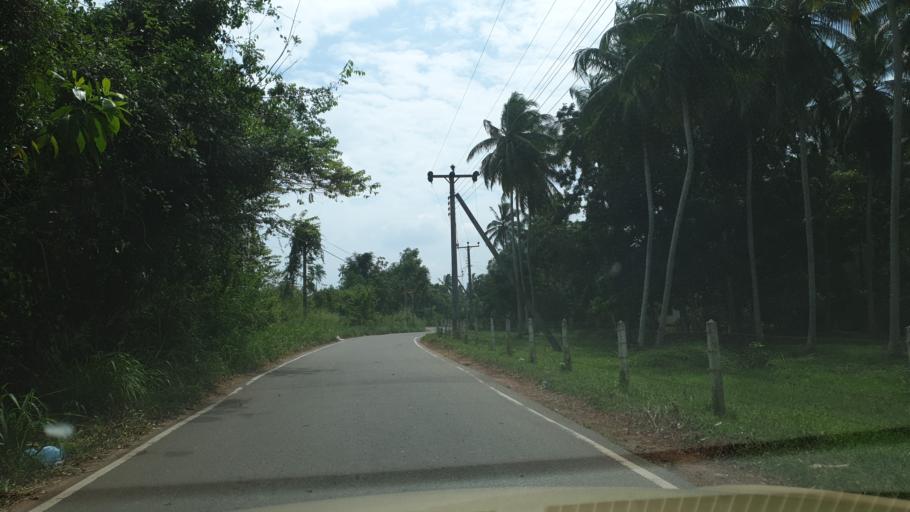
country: LK
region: North Western
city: Kuliyapitiya
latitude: 7.3528
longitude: 79.9777
